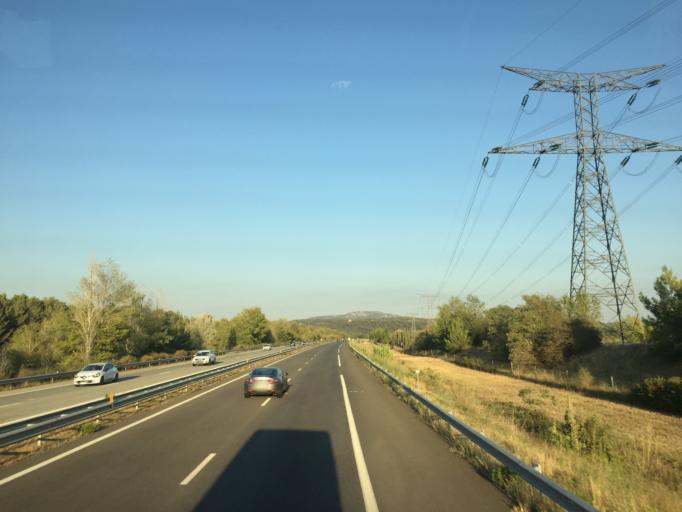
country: FR
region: Provence-Alpes-Cote d'Azur
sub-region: Departement des Bouches-du-Rhone
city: Peyrolles-en-Provence
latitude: 43.6584
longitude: 5.5834
